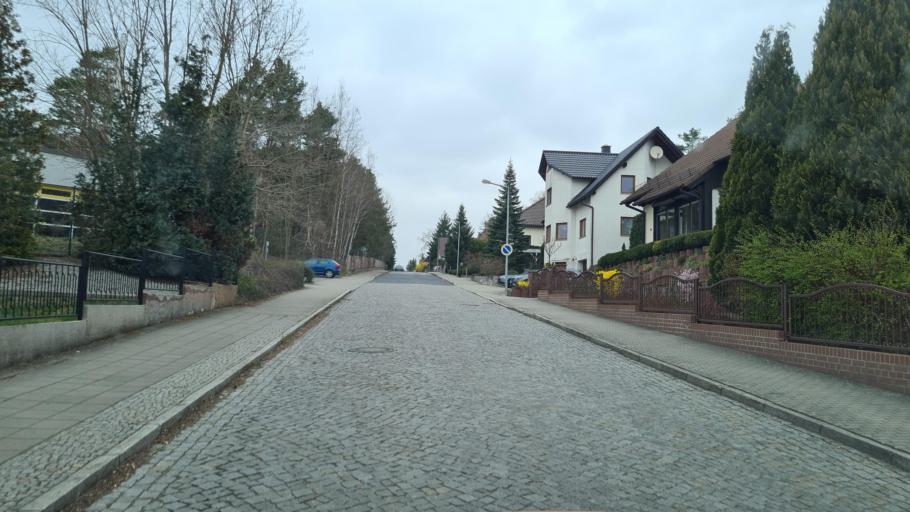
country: DE
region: Brandenburg
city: Lauchhammer
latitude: 51.4991
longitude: 13.7904
